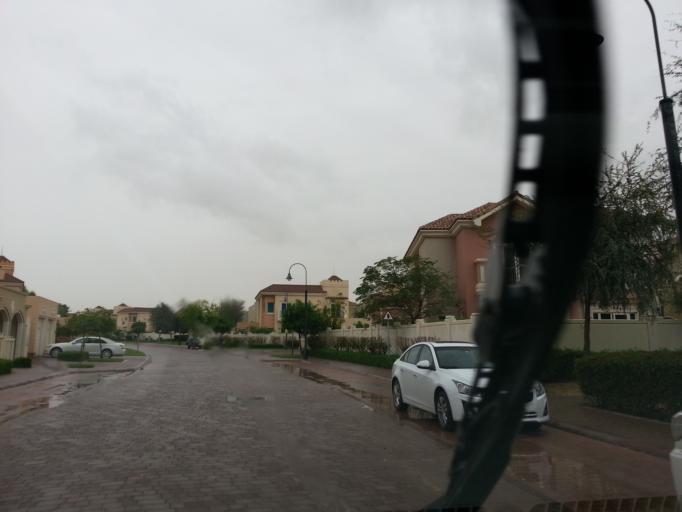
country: AE
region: Dubai
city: Dubai
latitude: 25.0286
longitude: 55.2104
